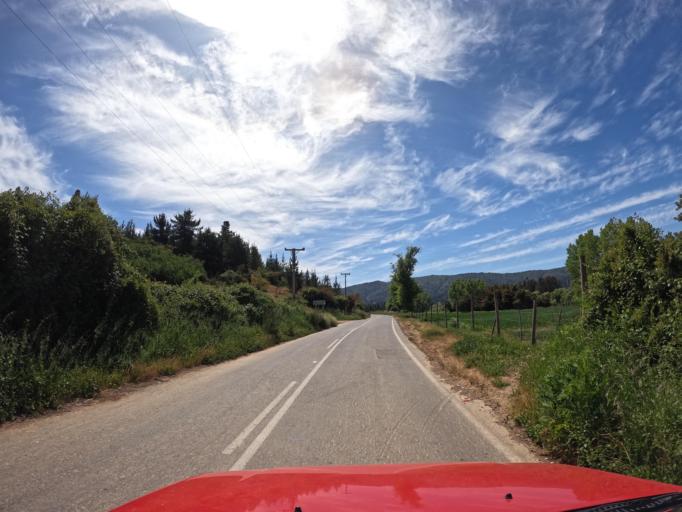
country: CL
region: Maule
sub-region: Provincia de Talca
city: Constitucion
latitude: -34.9989
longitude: -71.9871
